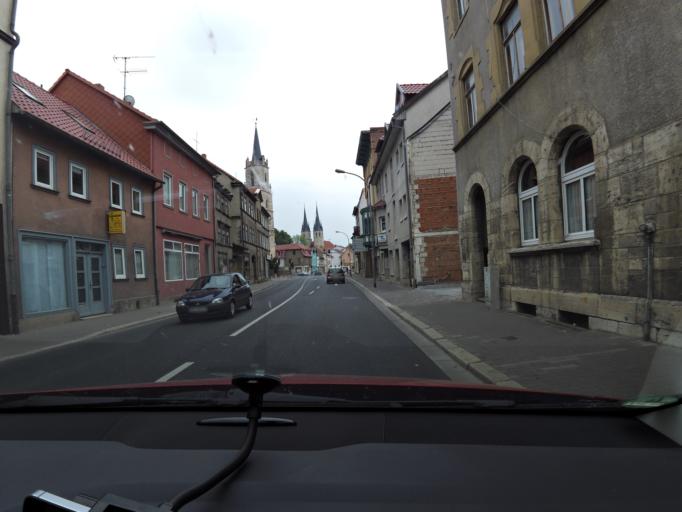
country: DE
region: Thuringia
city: Muehlhausen
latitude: 51.2061
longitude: 10.4500
